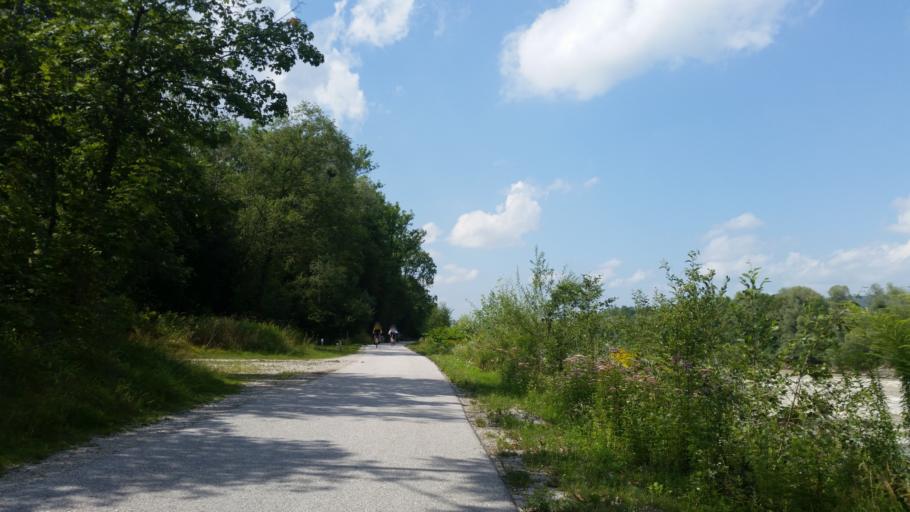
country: AT
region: Salzburg
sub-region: Politischer Bezirk Salzburg-Umgebung
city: Bergheim
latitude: 47.8446
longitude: 13.0118
